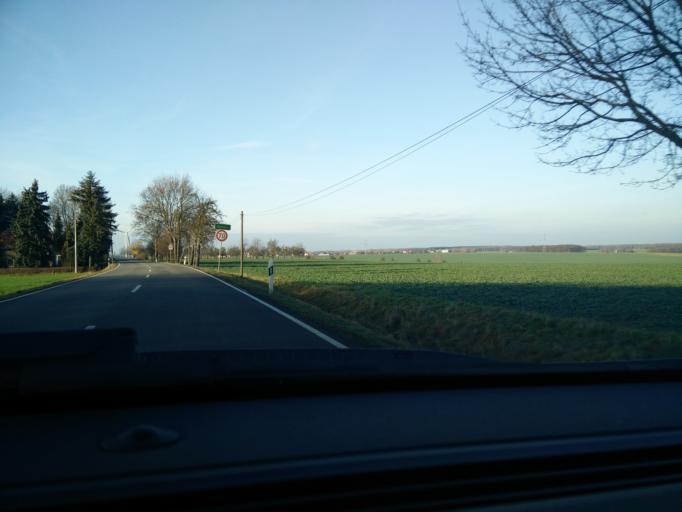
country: DE
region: Saxony
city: Geithain
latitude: 51.0832
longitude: 12.7177
